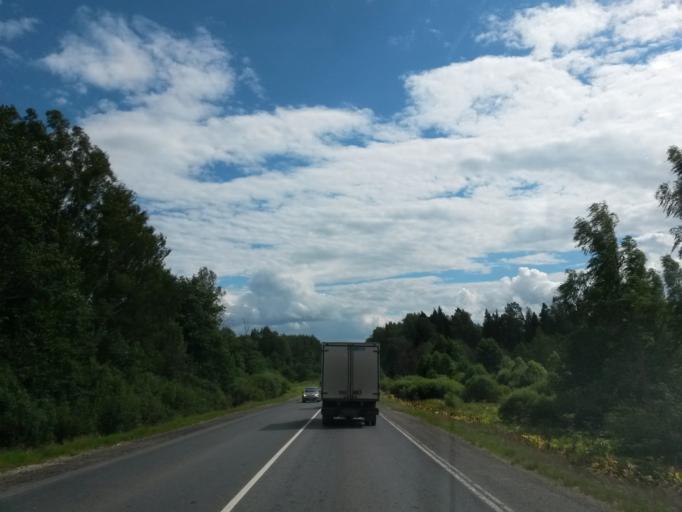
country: RU
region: Ivanovo
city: Novo-Talitsy
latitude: 57.0608
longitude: 40.7198
